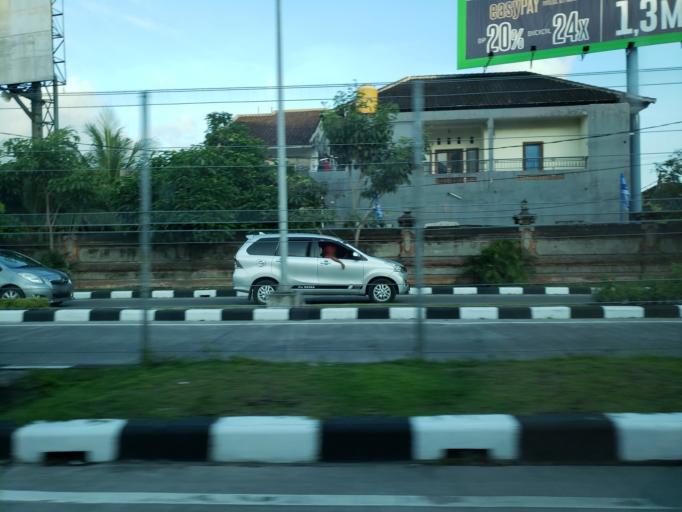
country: ID
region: Bali
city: Kelanabian
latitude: -8.7427
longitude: 115.1677
